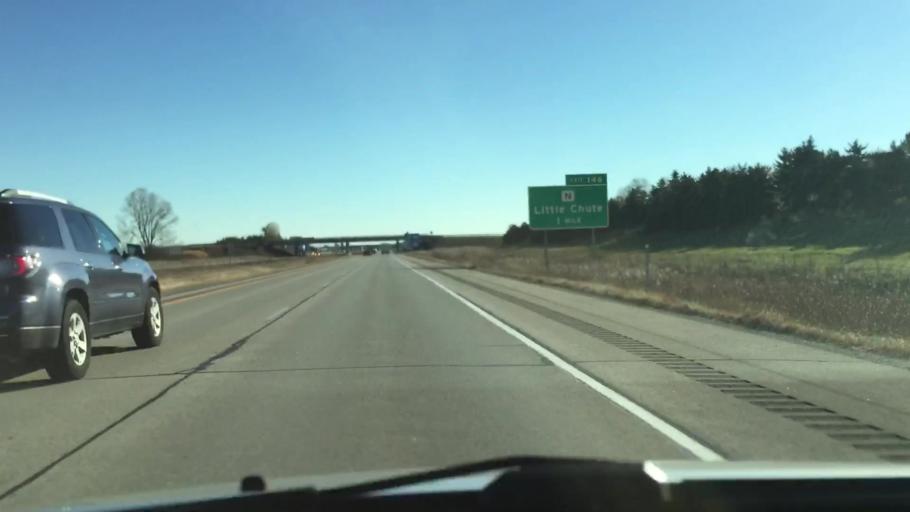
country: US
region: Wisconsin
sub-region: Outagamie County
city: Kimberly
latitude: 44.2978
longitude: -88.3379
